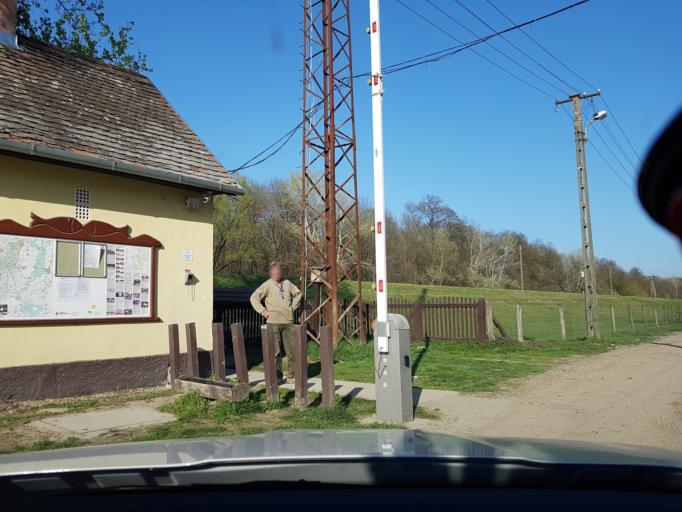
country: HU
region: Tolna
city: Bogyiszlo
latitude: 46.3279
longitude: 18.8532
